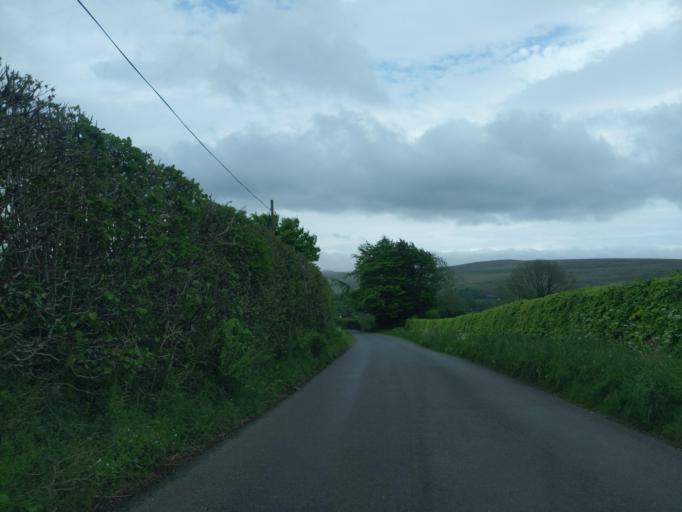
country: GB
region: England
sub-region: Devon
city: Tavistock
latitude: 50.6115
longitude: -4.1534
